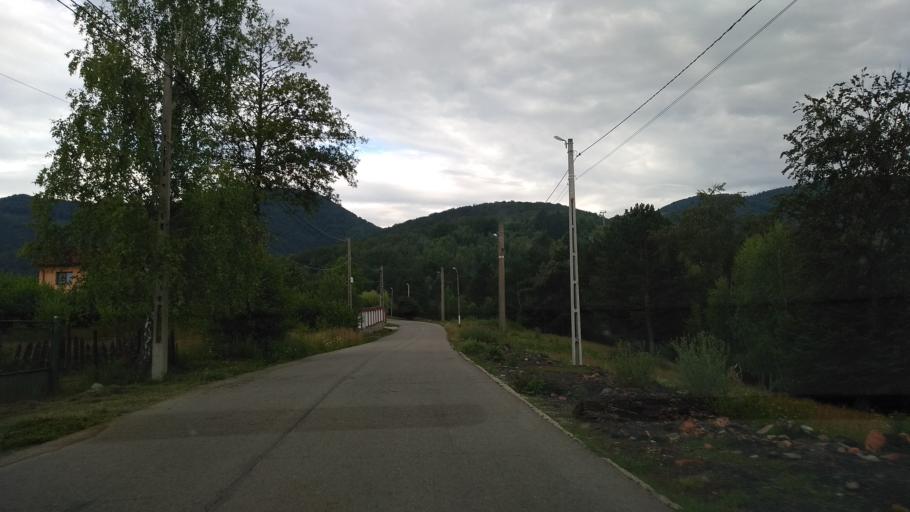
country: RO
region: Hunedoara
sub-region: Municipiul  Vulcan
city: Jiu-Paroseni
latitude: 45.3575
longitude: 23.2885
